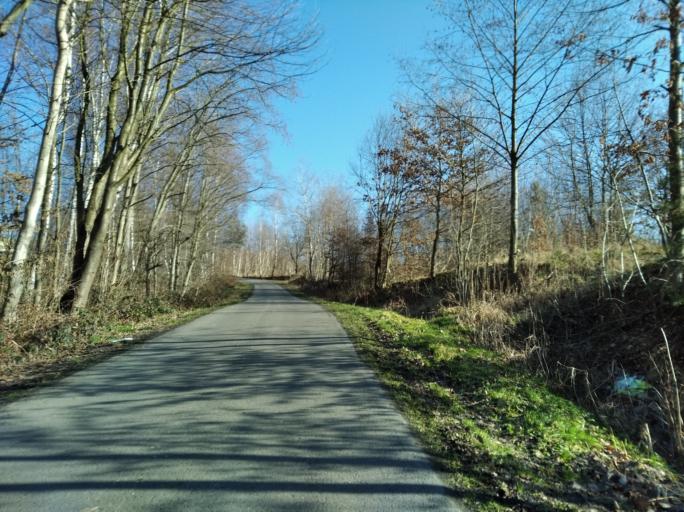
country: PL
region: Subcarpathian Voivodeship
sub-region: Powiat strzyzowski
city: Konieczkowa
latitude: 49.8574
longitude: 21.9338
